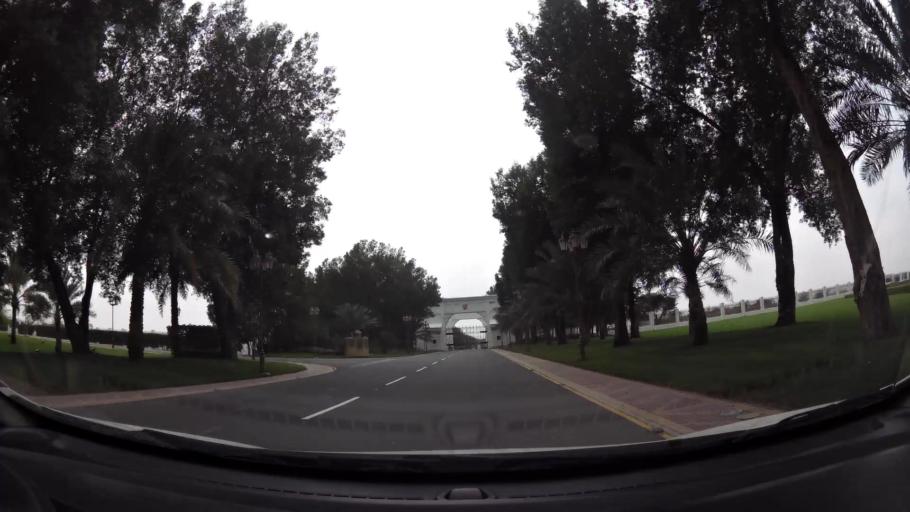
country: BH
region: Central Governorate
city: Dar Kulayb
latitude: 26.0706
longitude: 50.5278
